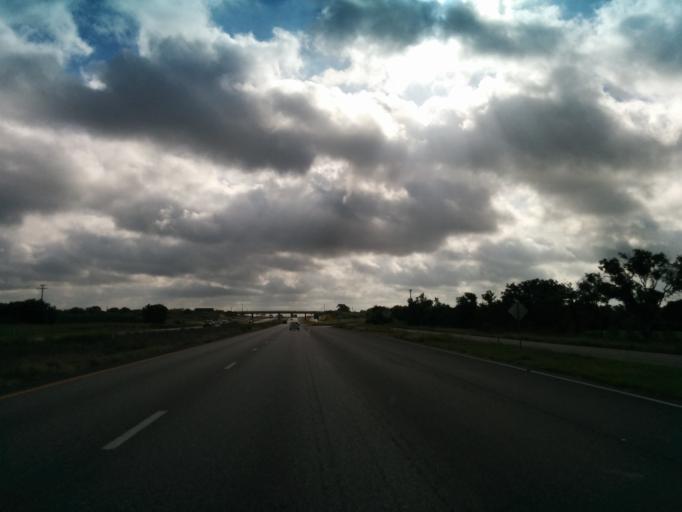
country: US
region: Texas
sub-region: Guadalupe County
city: Marion
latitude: 29.5063
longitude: -98.1722
